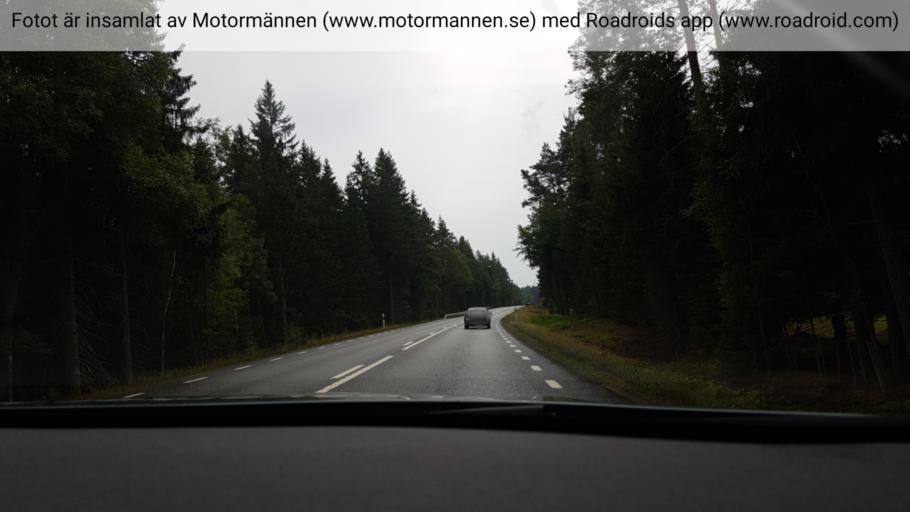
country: SE
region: Joenkoeping
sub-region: Savsjo Kommun
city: Vrigstad
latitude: 57.3809
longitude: 14.4017
